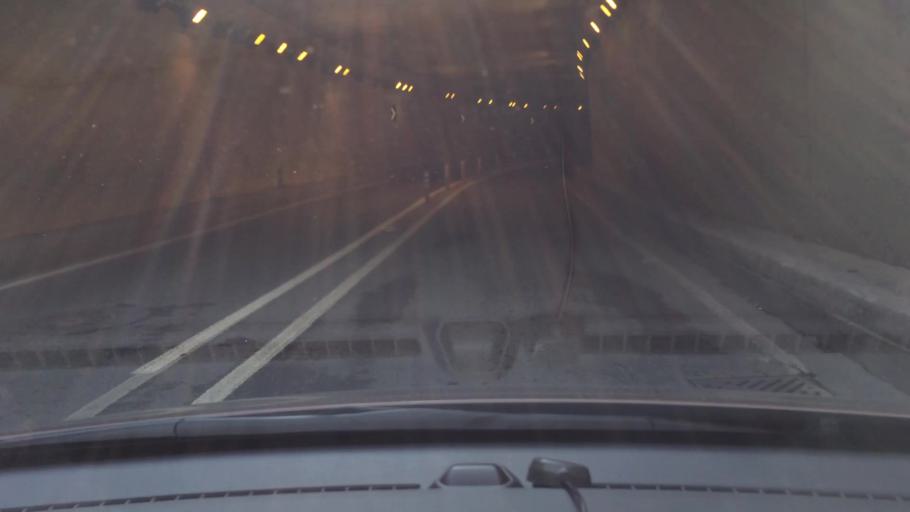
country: TR
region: Istanbul
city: Eminoenue
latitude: 41.0112
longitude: 28.9654
